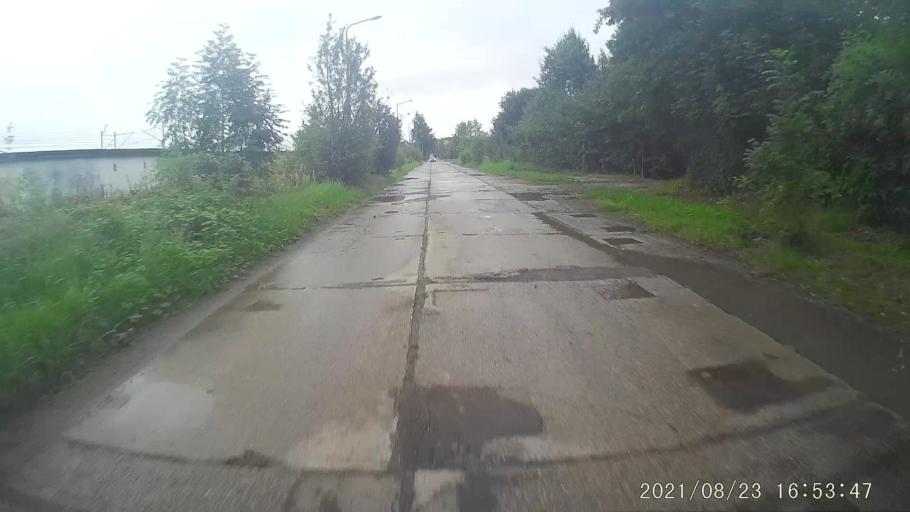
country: PL
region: Lower Silesian Voivodeship
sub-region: Powiat zgorzelecki
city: Zgorzelec
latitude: 51.1612
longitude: 15.0188
